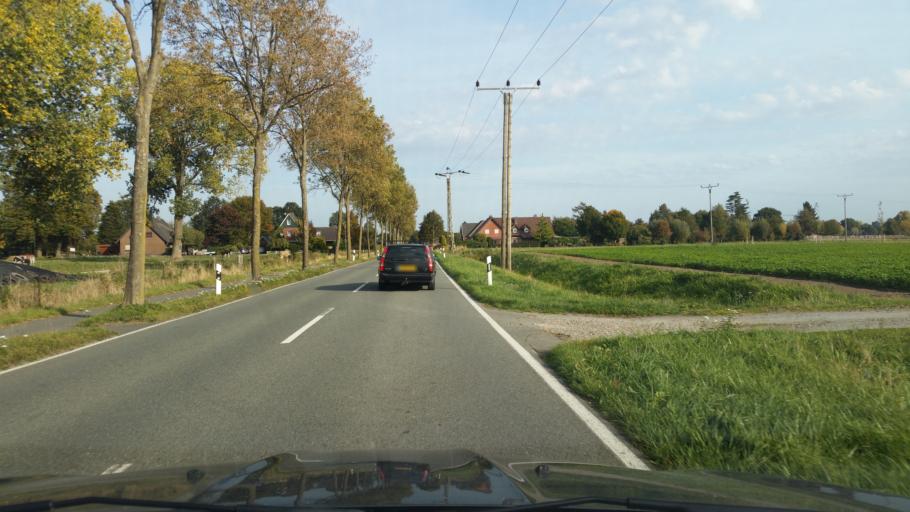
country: DE
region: North Rhine-Westphalia
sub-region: Regierungsbezirk Dusseldorf
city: Bocholt
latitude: 51.8478
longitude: 6.5632
